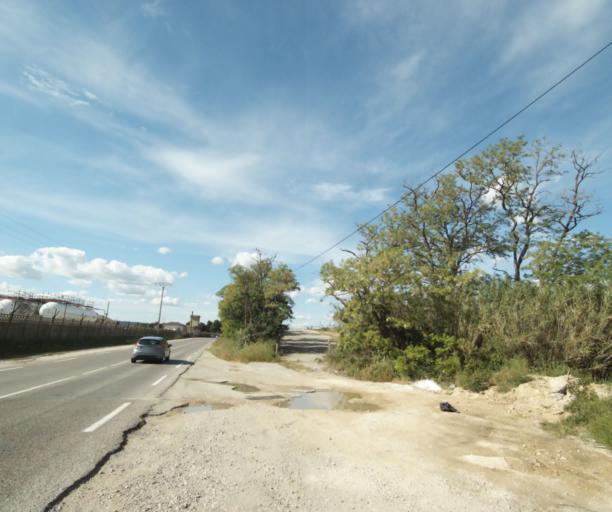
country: FR
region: Provence-Alpes-Cote d'Azur
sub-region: Departement des Bouches-du-Rhone
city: Rognac
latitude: 43.4798
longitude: 5.2307
